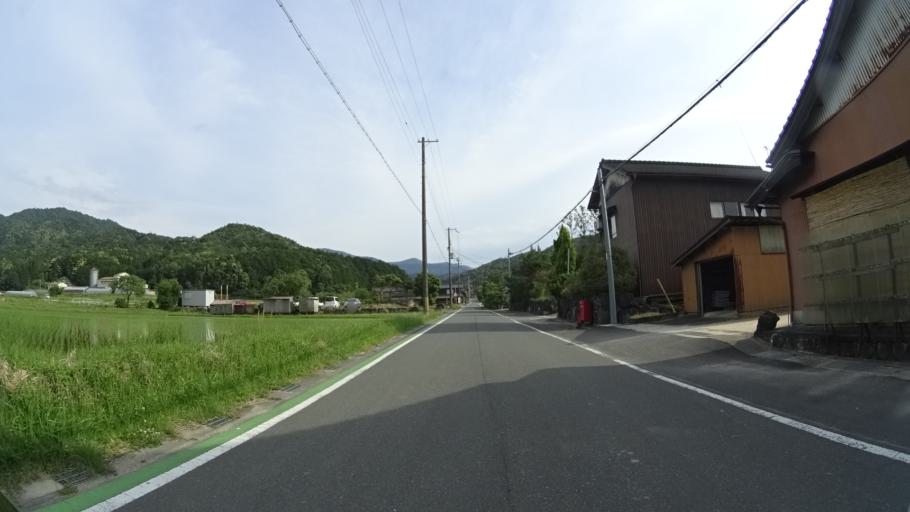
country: JP
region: Kyoto
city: Miyazu
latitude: 35.5259
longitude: 135.1266
